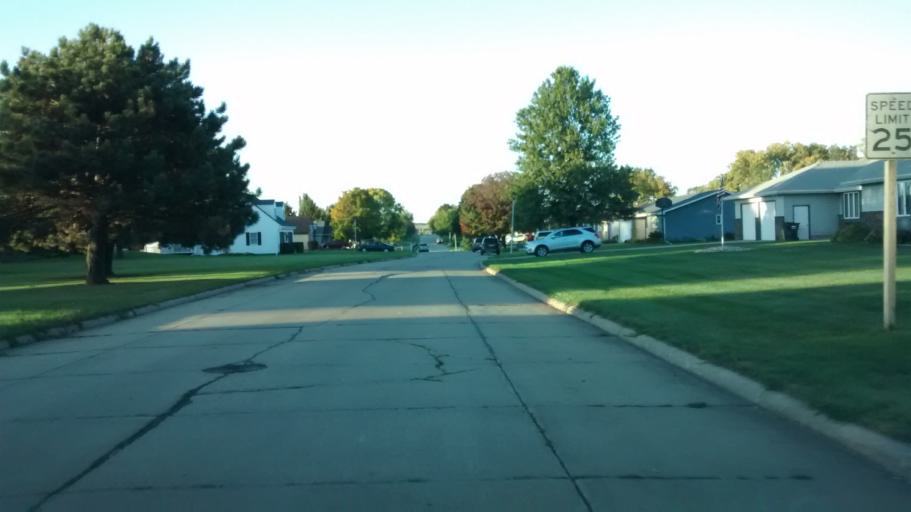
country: US
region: Iowa
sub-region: Woodbury County
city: Moville
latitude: 42.4912
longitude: -96.0667
